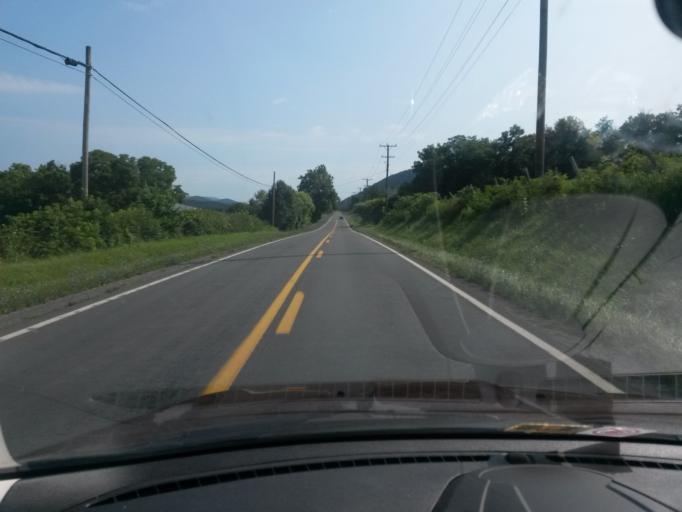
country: US
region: Virginia
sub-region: Shenandoah County
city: Basye
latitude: 38.9361
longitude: -78.8204
